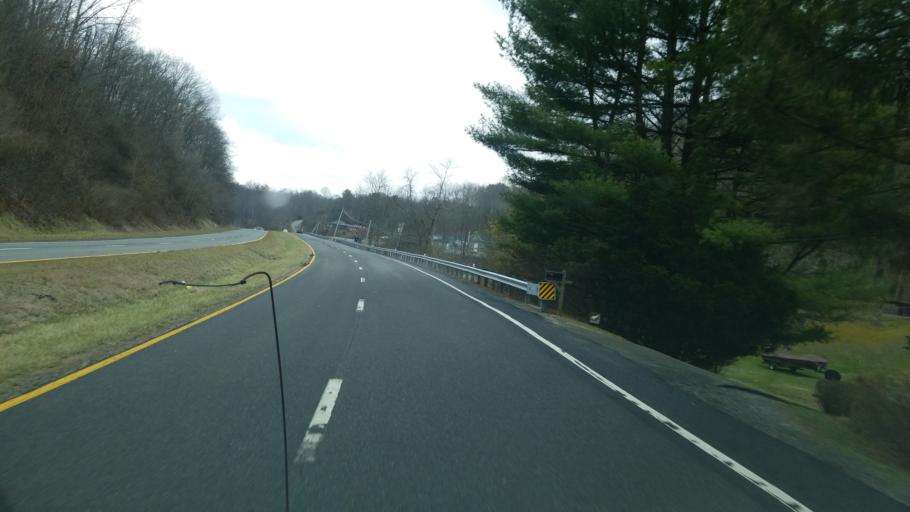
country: US
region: Virginia
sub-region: Giles County
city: Pearisburg
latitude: 37.2719
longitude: -80.7338
